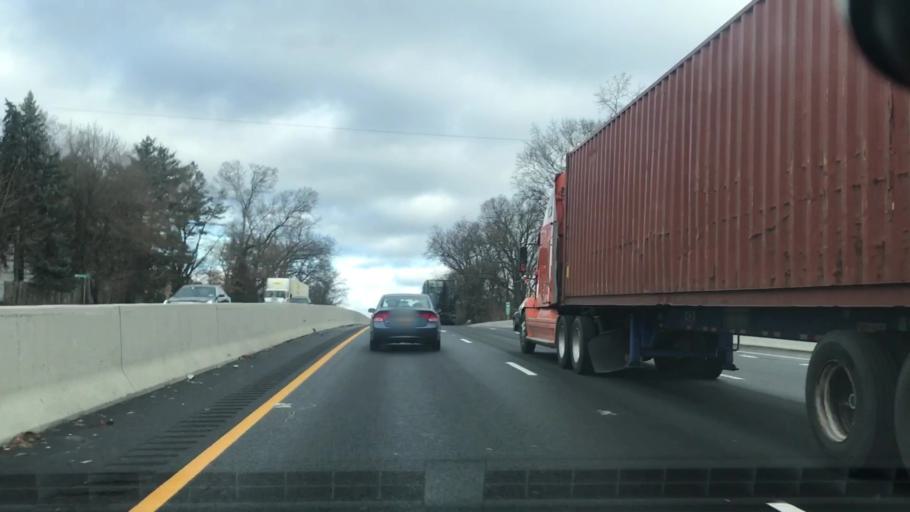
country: US
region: New Jersey
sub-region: Bergen County
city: Waldwick
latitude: 41.0127
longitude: -74.1071
